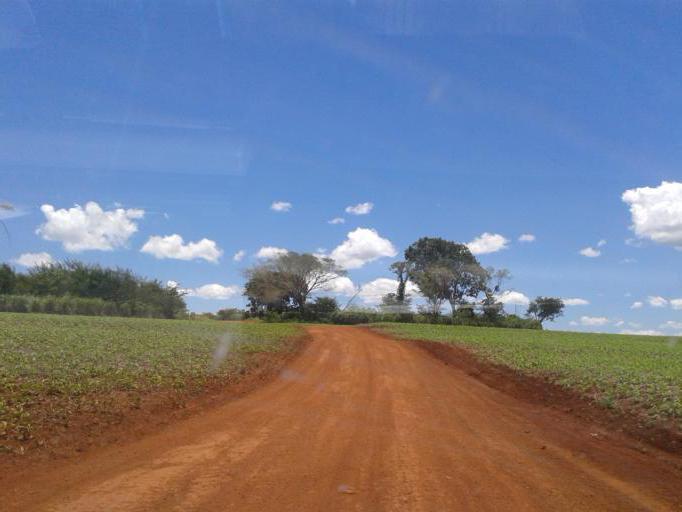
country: BR
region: Minas Gerais
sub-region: Capinopolis
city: Capinopolis
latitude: -18.5889
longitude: -49.5425
